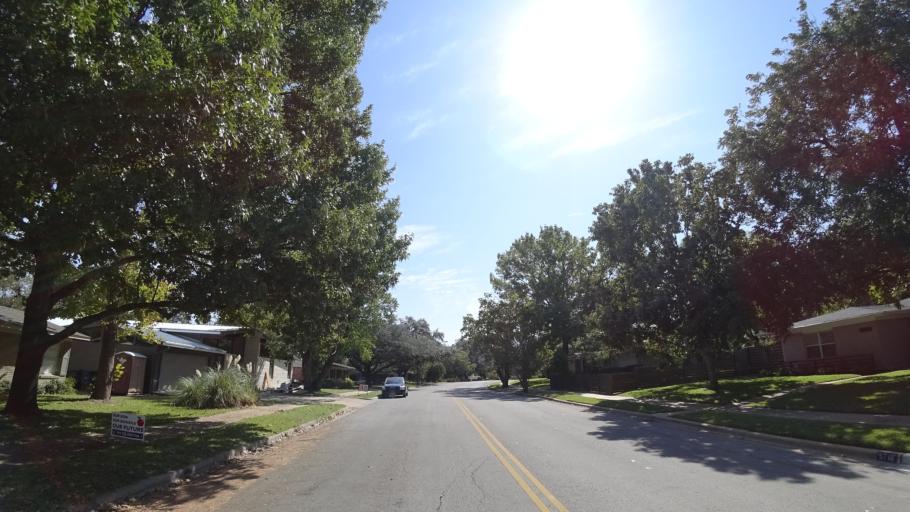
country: US
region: Texas
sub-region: Travis County
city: West Lake Hills
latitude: 30.3368
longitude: -97.7529
